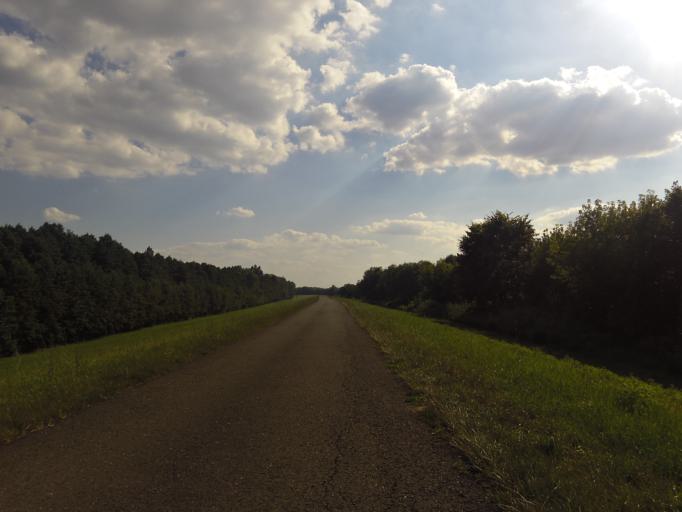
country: HU
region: Jasz-Nagykun-Szolnok
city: Abadszalok
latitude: 47.5216
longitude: 20.5953
